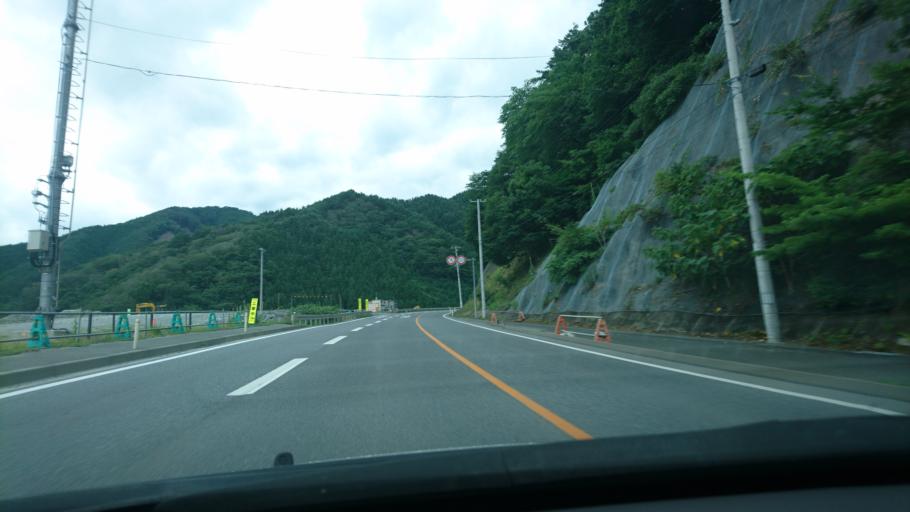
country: JP
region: Iwate
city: Kamaishi
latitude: 39.2159
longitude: 141.8744
